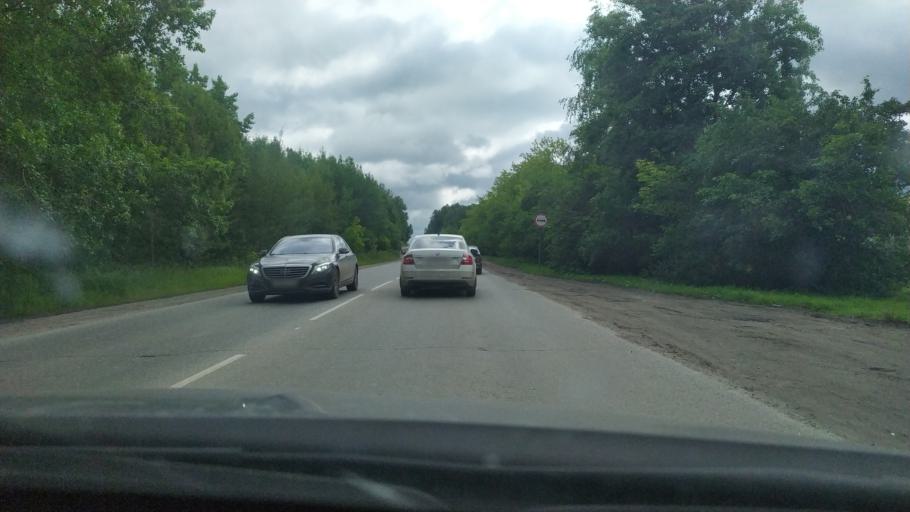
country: RU
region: Perm
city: Froly
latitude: 57.9752
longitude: 56.3253
